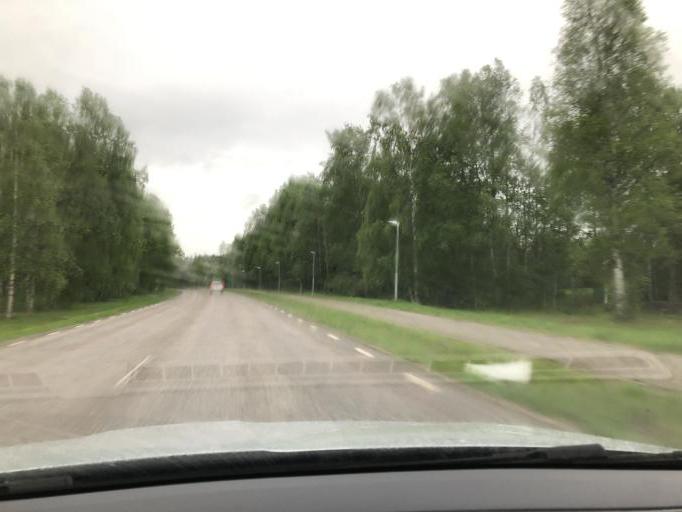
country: SE
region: Norrbotten
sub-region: Pitea Kommun
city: Bergsviken
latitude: 65.3371
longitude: 21.4105
